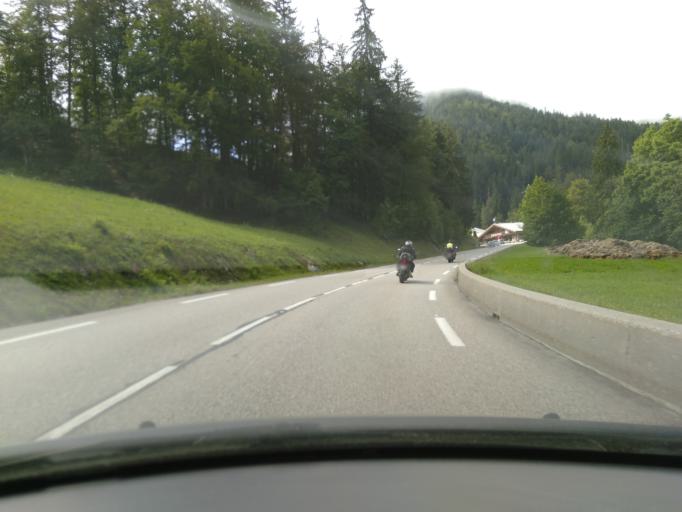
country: FR
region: Rhone-Alpes
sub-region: Departement de la Haute-Savoie
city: Saint-Jean-de-Sixt
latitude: 45.9162
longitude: 6.4198
